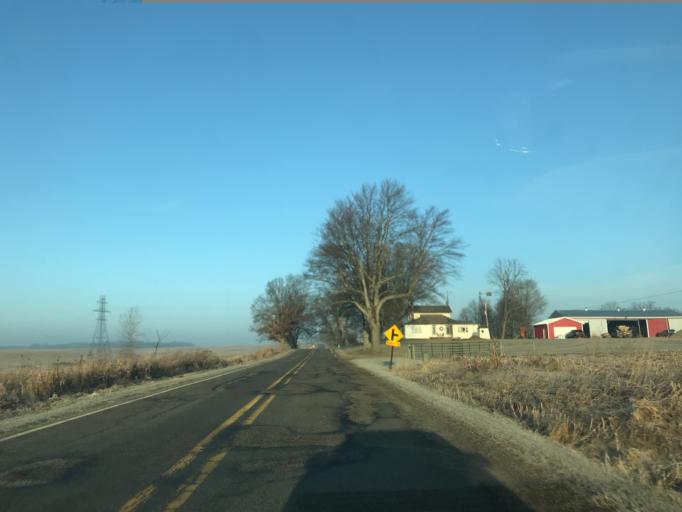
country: US
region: Michigan
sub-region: Ingham County
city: Leslie
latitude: 42.4092
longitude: -84.4942
